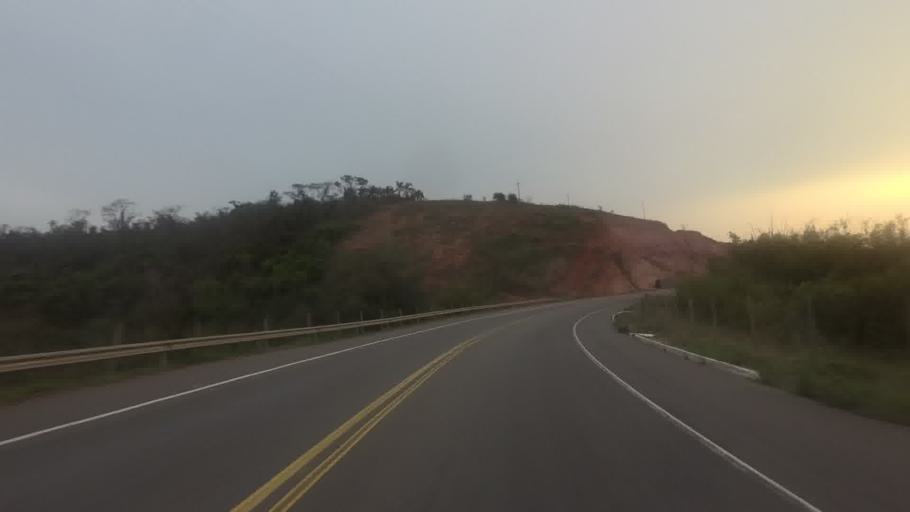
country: BR
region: Minas Gerais
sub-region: Recreio
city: Recreio
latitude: -21.7322
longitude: -42.4453
